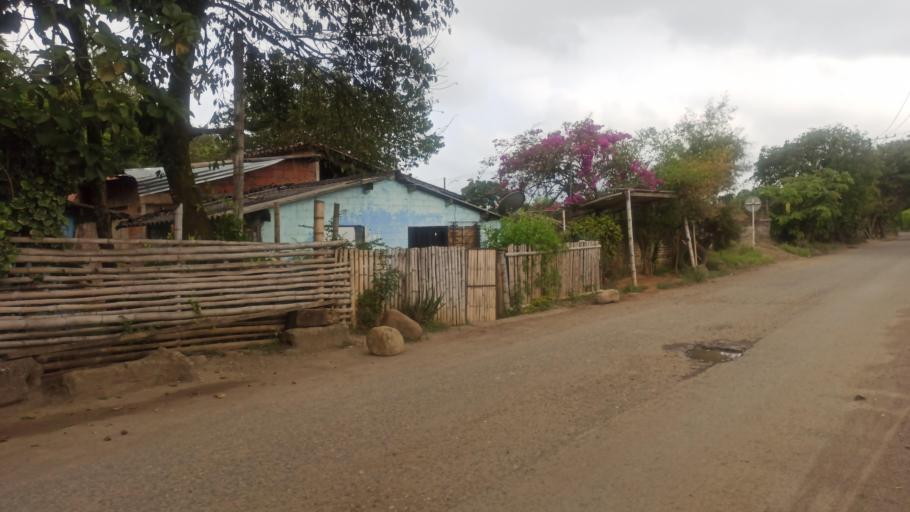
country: CO
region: Valle del Cauca
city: Jamundi
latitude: 3.2013
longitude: -76.5101
